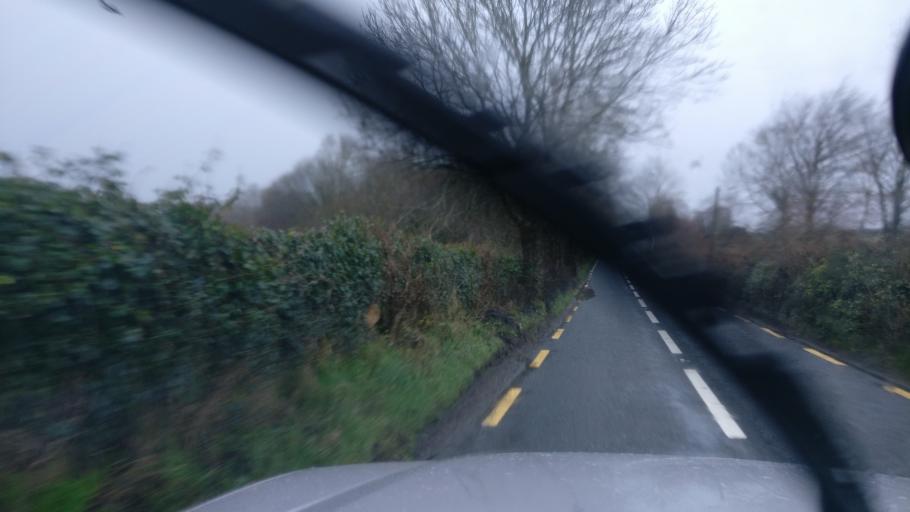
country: IE
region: Connaught
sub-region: County Galway
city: Loughrea
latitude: 53.1555
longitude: -8.4808
